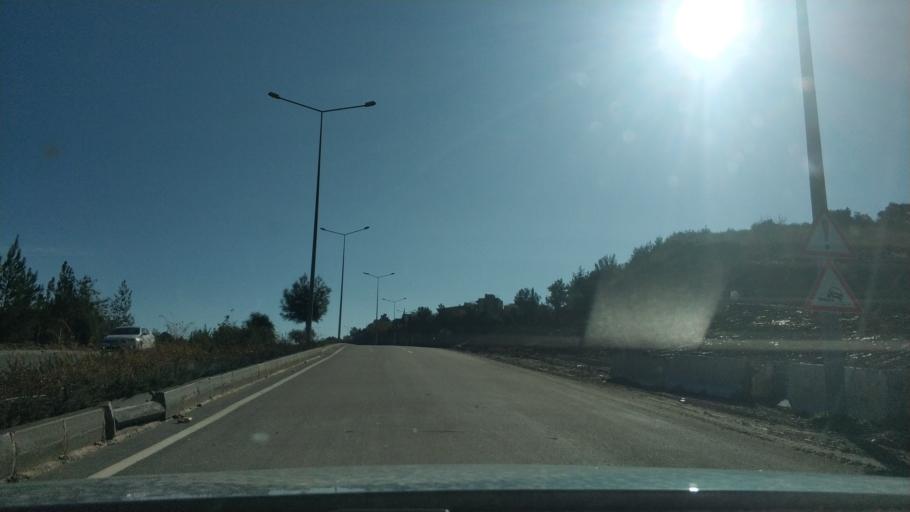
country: TR
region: Adana
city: Seyhan
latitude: 37.0655
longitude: 35.2693
